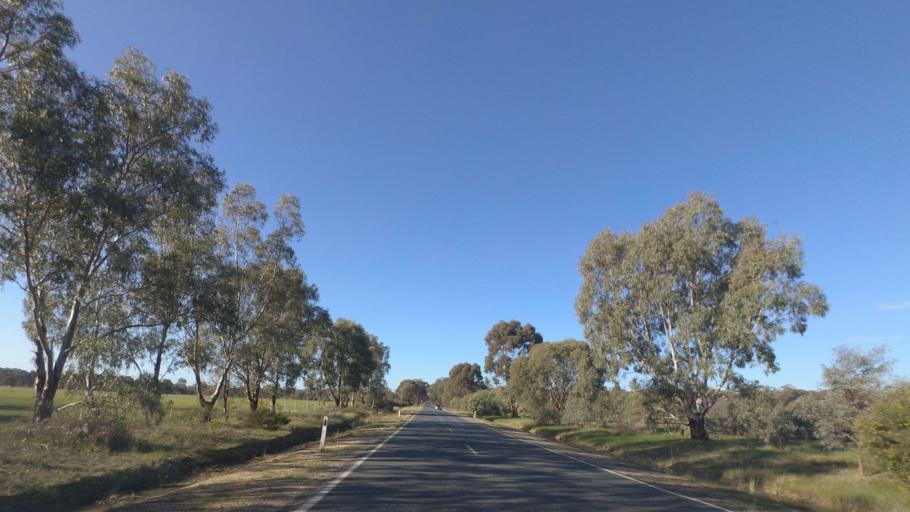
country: AU
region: Victoria
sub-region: Greater Bendigo
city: Epsom
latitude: -36.6751
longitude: 144.3965
